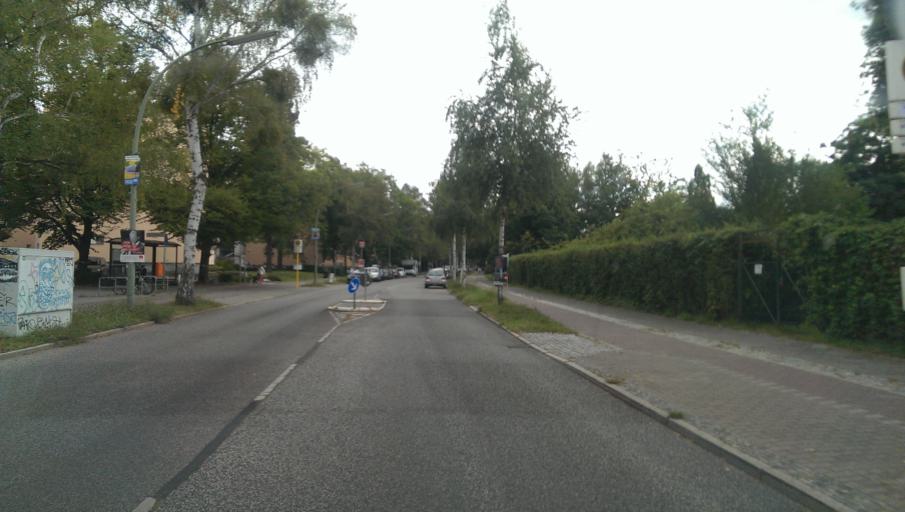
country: DE
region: Brandenburg
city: Teltow
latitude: 52.4151
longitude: 13.2513
